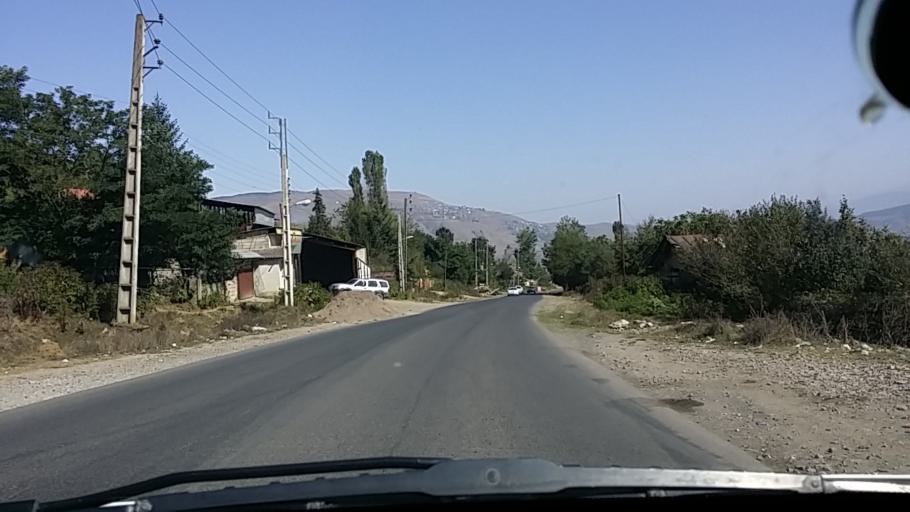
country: IR
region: Mazandaran
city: `Abbasabad
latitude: 36.5515
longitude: 51.1658
